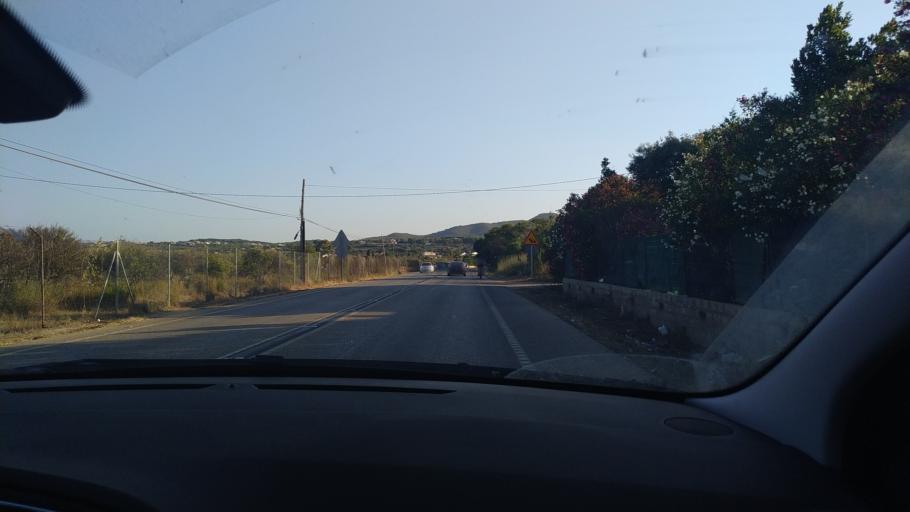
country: ES
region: Valencia
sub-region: Provincia de Alicante
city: Javea
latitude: 38.7786
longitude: 0.1479
